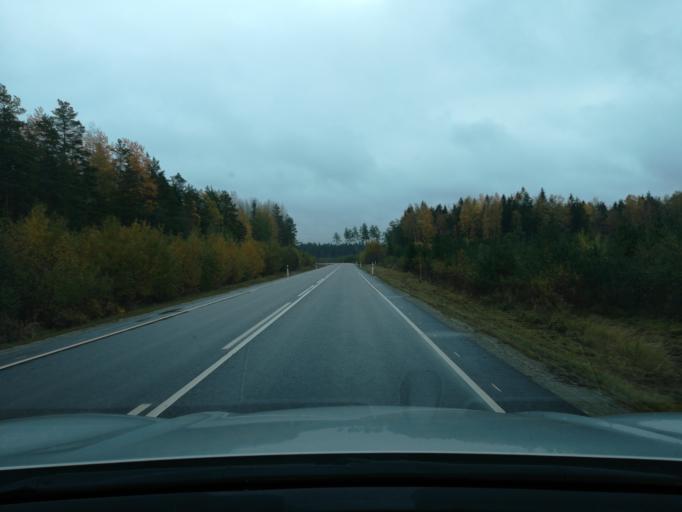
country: EE
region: Ida-Virumaa
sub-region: Johvi vald
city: Johvi
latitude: 59.3027
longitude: 27.4671
